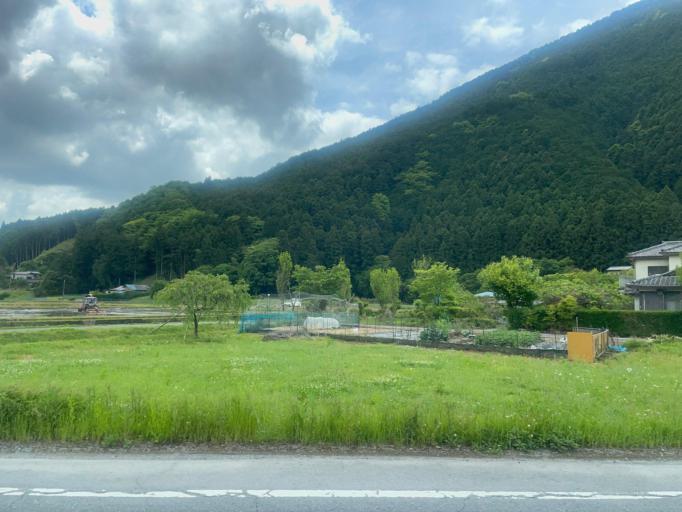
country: JP
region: Tochigi
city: Tanuma
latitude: 36.4696
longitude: 139.6309
